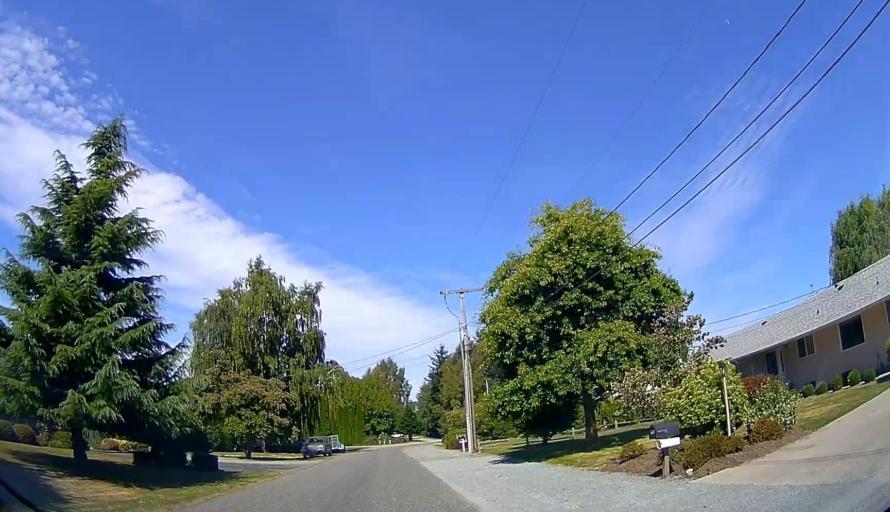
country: US
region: Washington
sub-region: Skagit County
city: Mount Vernon
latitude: 48.4237
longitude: -122.3627
